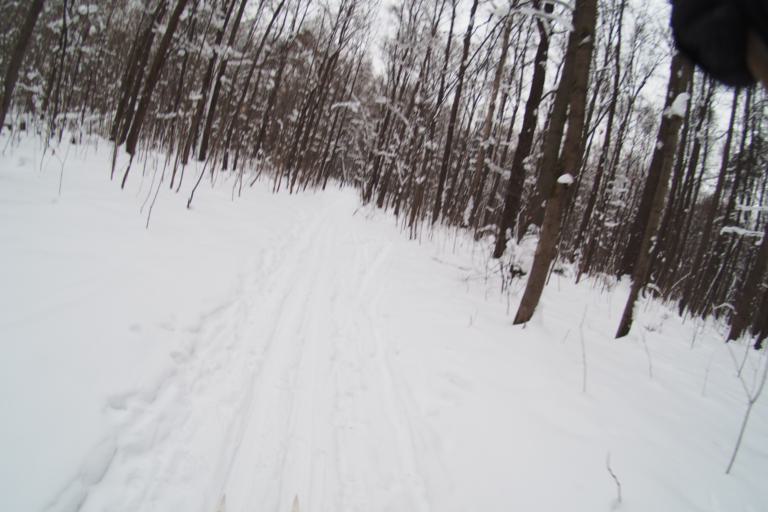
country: RU
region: Moskovskaya
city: Izmaylovo
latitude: 55.7760
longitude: 37.7852
